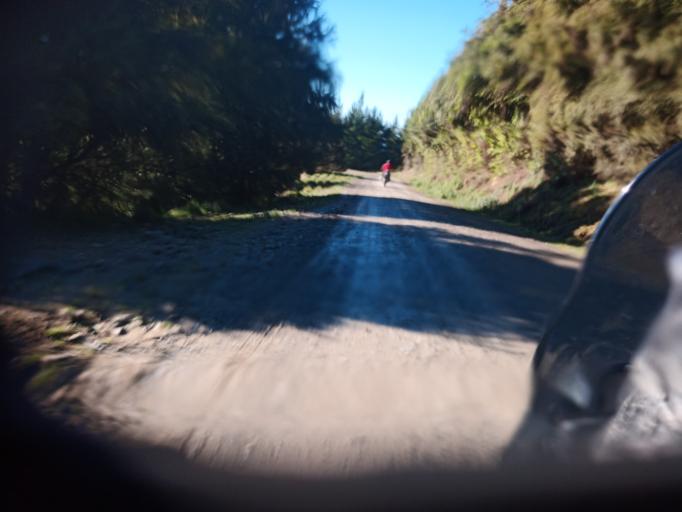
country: NZ
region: Gisborne
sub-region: Gisborne District
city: Gisborne
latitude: -38.1973
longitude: 178.0806
